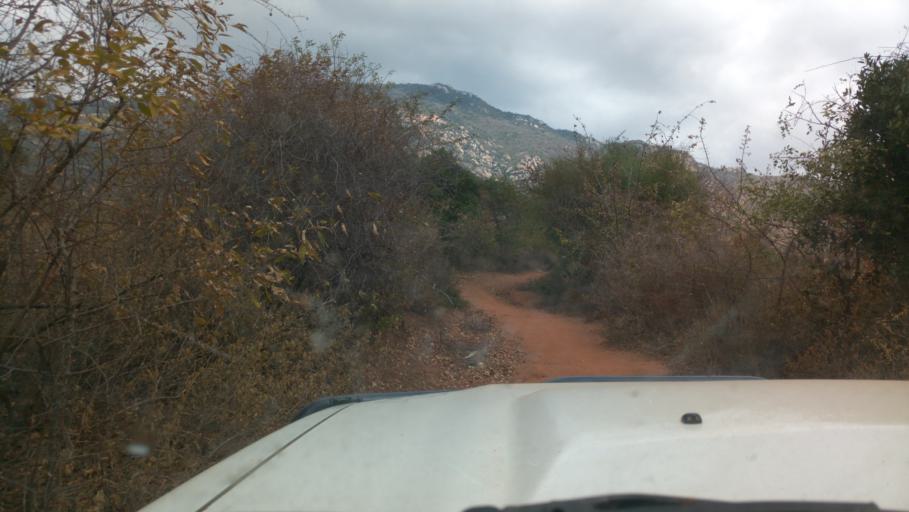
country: KE
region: Kitui
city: Kitui
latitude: -1.8685
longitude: 38.3663
